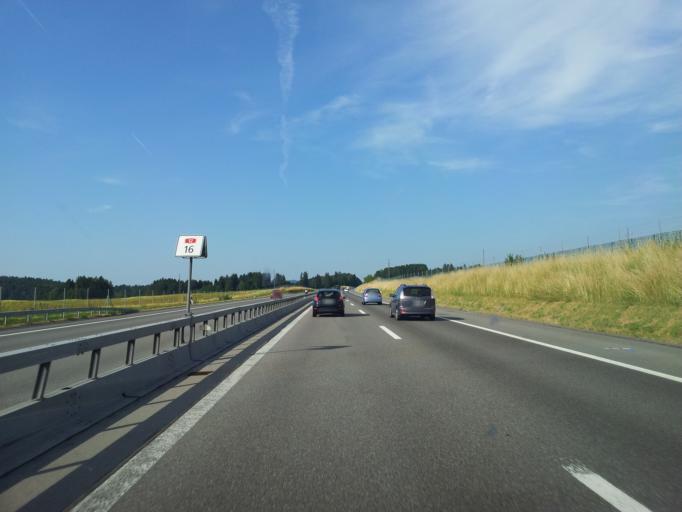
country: CH
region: Fribourg
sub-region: Gruyere District
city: Sales
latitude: 46.5940
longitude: 6.9373
